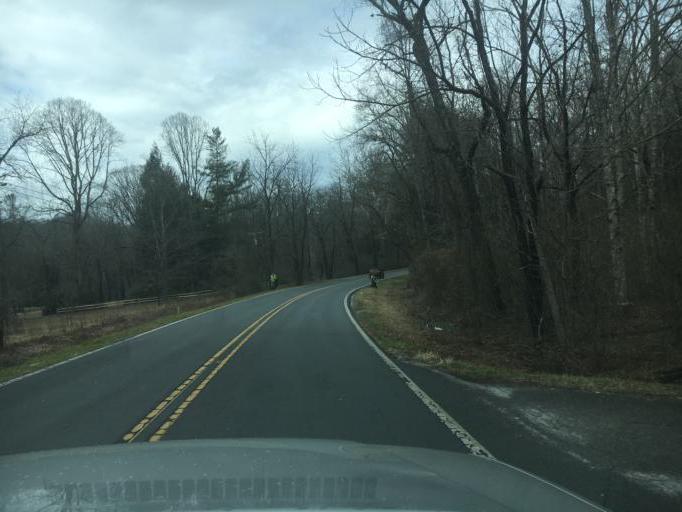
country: US
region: North Carolina
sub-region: Transylvania County
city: Brevard
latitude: 35.2755
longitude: -82.7109
